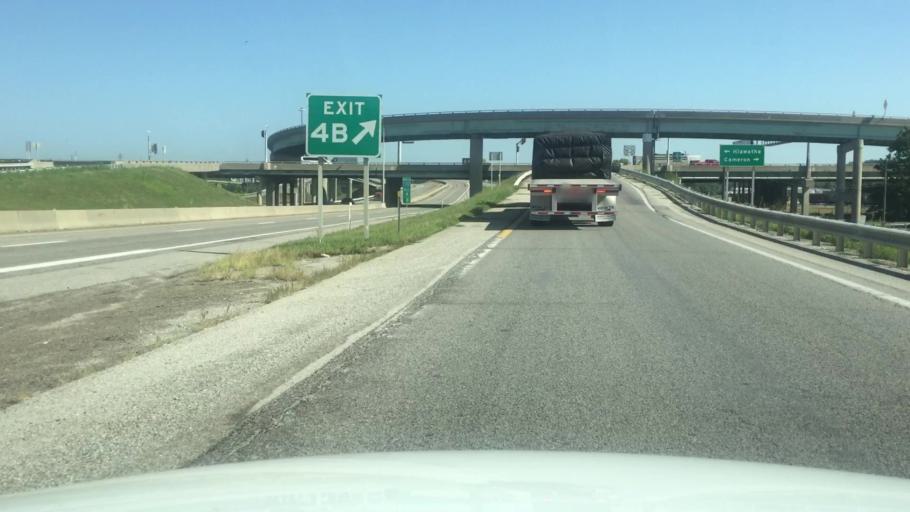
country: US
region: Kansas
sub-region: Doniphan County
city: Elwood
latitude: 39.7473
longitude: -94.8533
